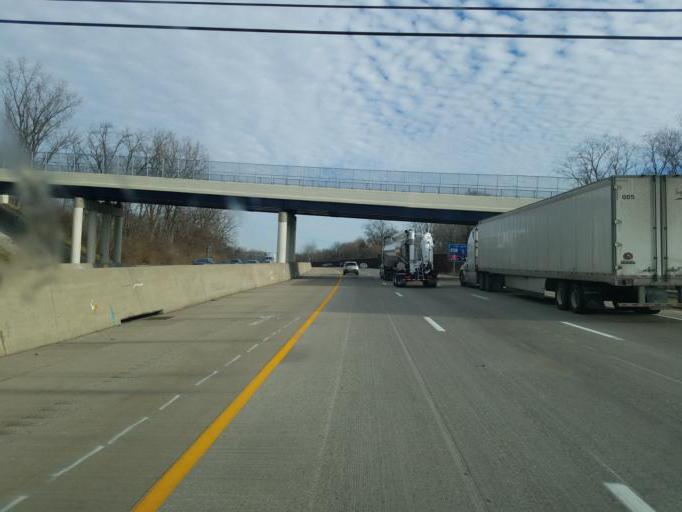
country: US
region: Ohio
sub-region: Montgomery County
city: Huber Heights
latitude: 39.8671
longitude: -84.1594
